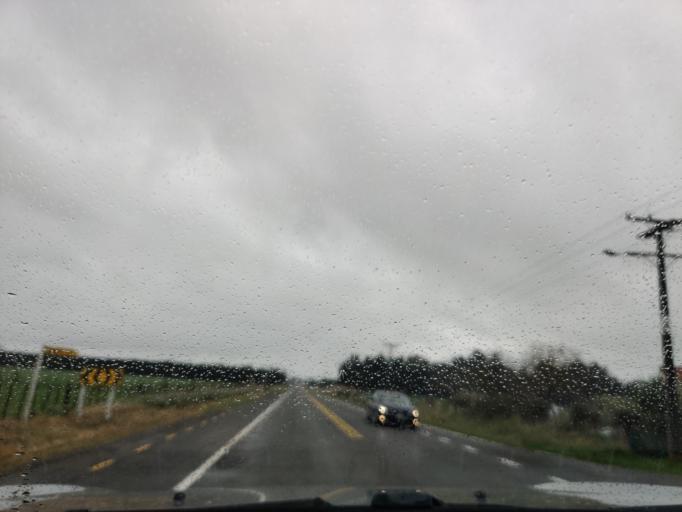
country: NZ
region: Hawke's Bay
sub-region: Hastings District
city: Hastings
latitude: -40.0176
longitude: 176.3504
